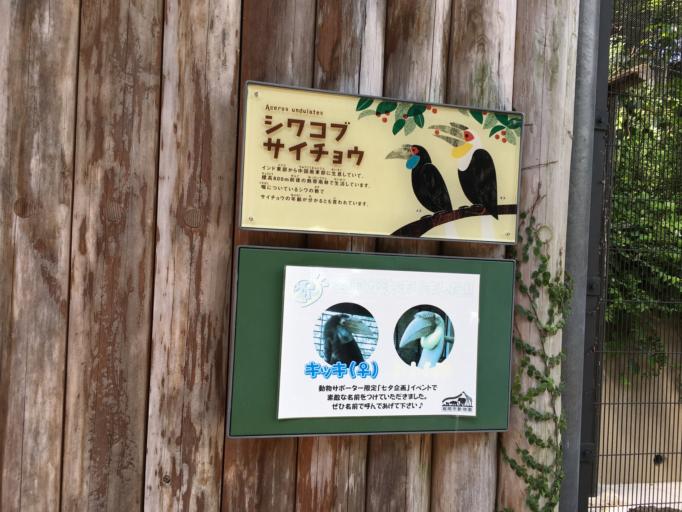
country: JP
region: Fukuoka
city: Fukuoka-shi
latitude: 33.5721
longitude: 130.3889
